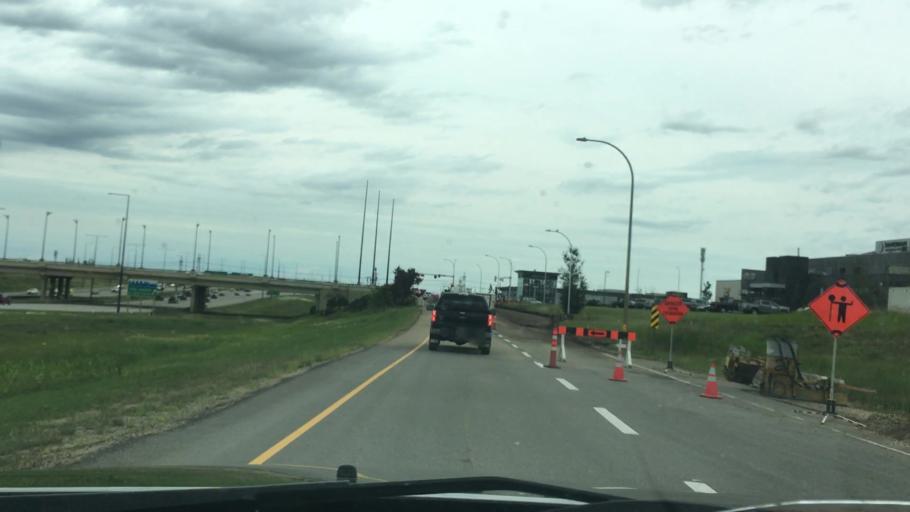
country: CA
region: Alberta
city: Beaumont
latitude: 53.4228
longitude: -113.4921
